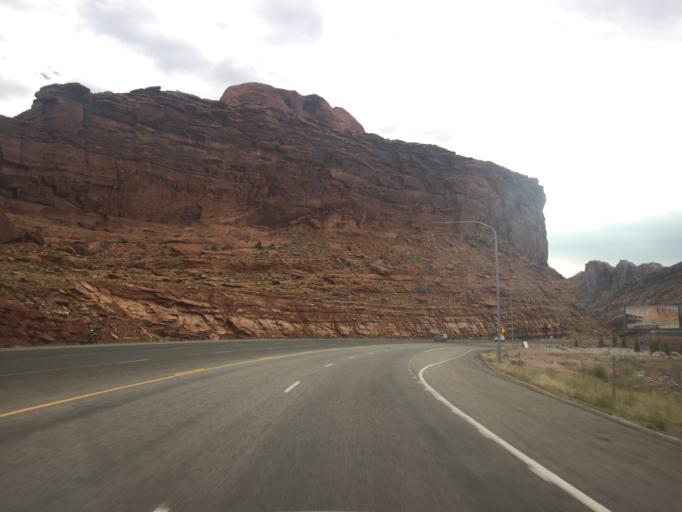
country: US
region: Utah
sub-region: Grand County
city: Moab
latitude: 38.6066
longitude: -109.5826
